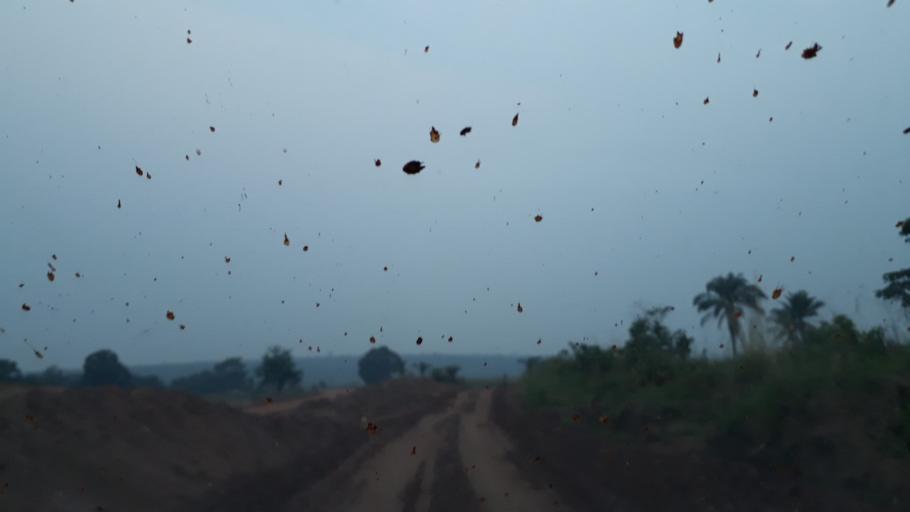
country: CD
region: Kasai-Occidental
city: Tshikapa
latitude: -6.4211
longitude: 20.6852
